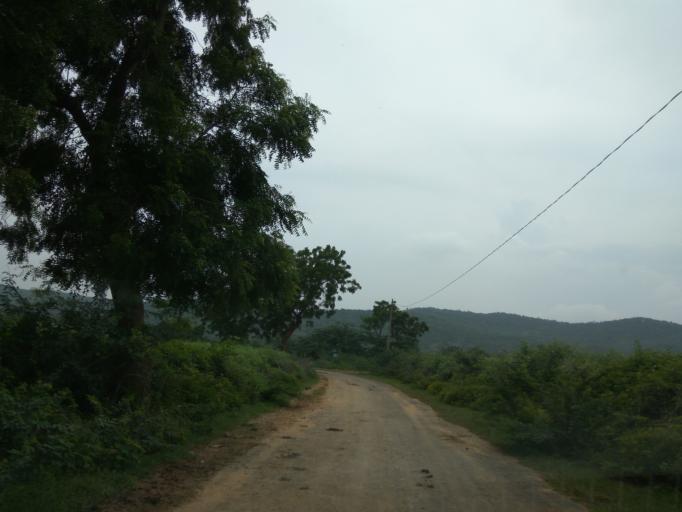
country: IN
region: Andhra Pradesh
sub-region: Prakasam
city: Cumbum
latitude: 15.4507
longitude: 79.0777
